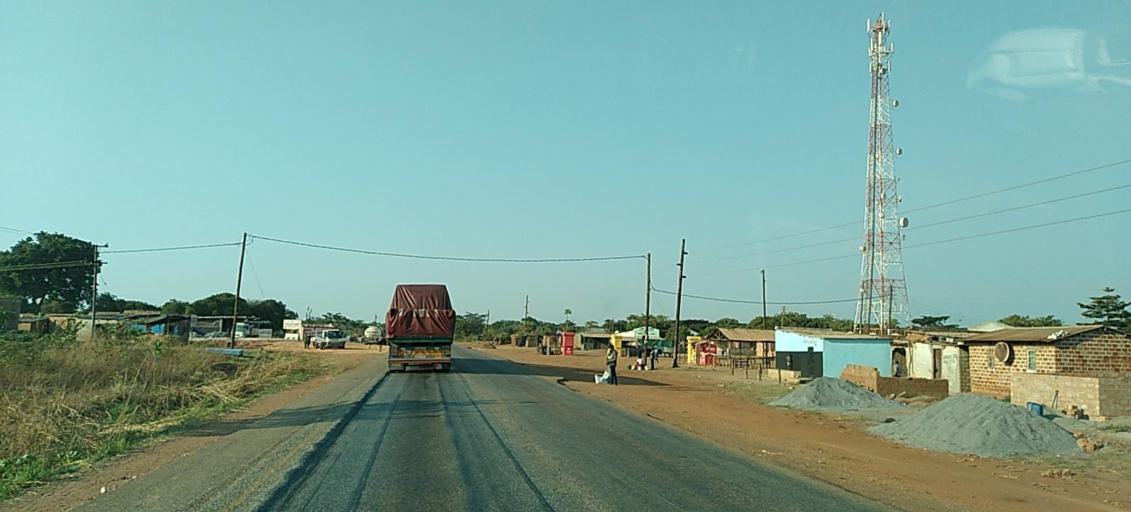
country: ZM
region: Copperbelt
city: Luanshya
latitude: -13.4696
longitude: 28.6736
